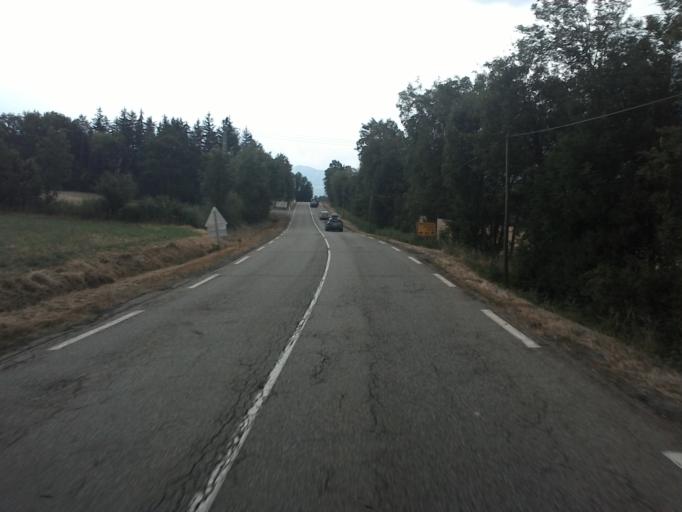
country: FR
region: Provence-Alpes-Cote d'Azur
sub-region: Departement des Hautes-Alpes
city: Saint-Bonnet-en-Champsaur
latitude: 44.7840
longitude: 5.9833
